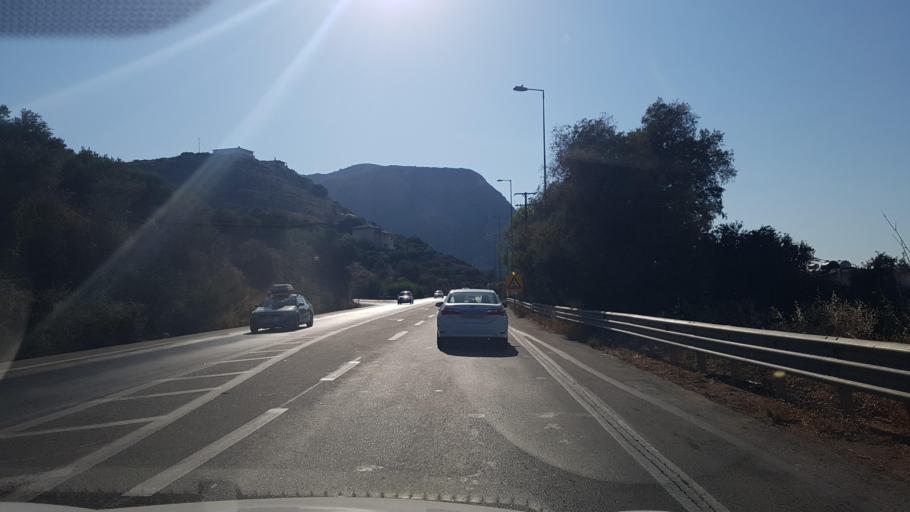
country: GR
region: Crete
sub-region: Nomos Chanias
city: Kalivai
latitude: 35.4683
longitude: 24.1268
